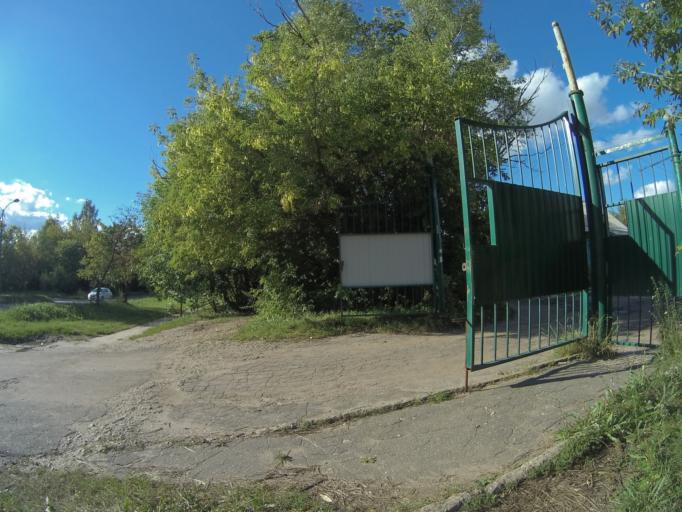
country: RU
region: Vladimir
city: Vladimir
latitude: 56.1552
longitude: 40.3656
